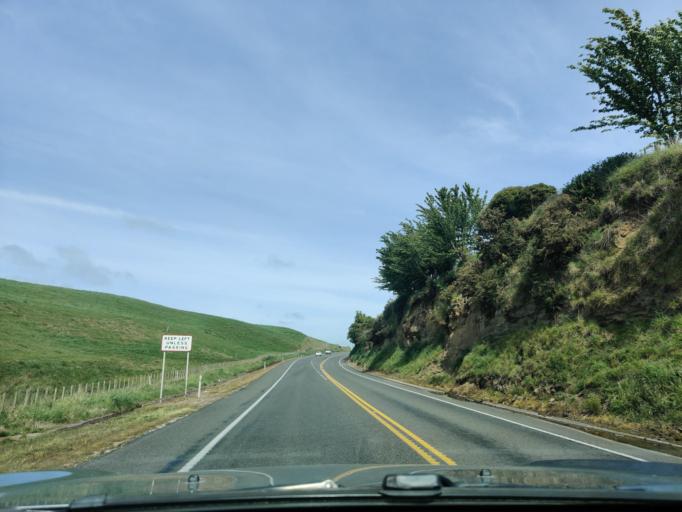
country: NZ
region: Taranaki
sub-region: South Taranaki District
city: Patea
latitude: -39.6863
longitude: 174.4197
